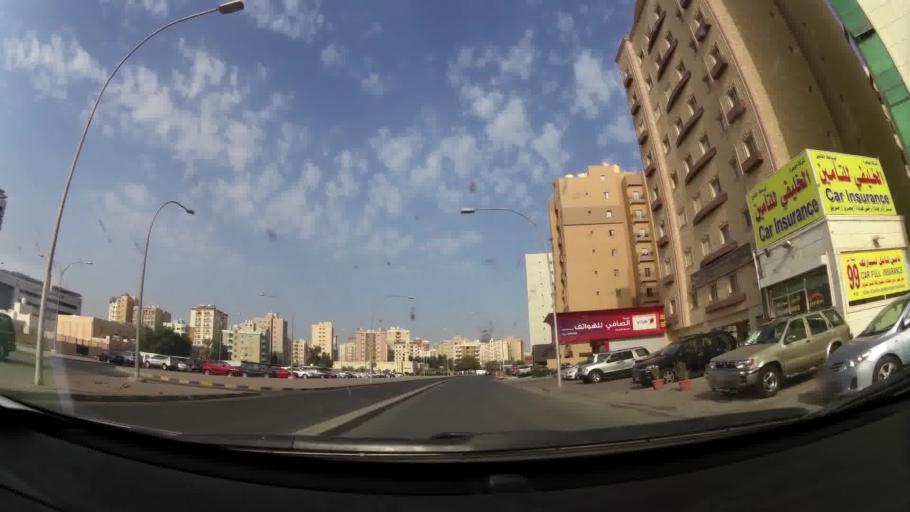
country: KW
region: Muhafazat Hawalli
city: As Salimiyah
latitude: 29.3316
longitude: 48.0837
